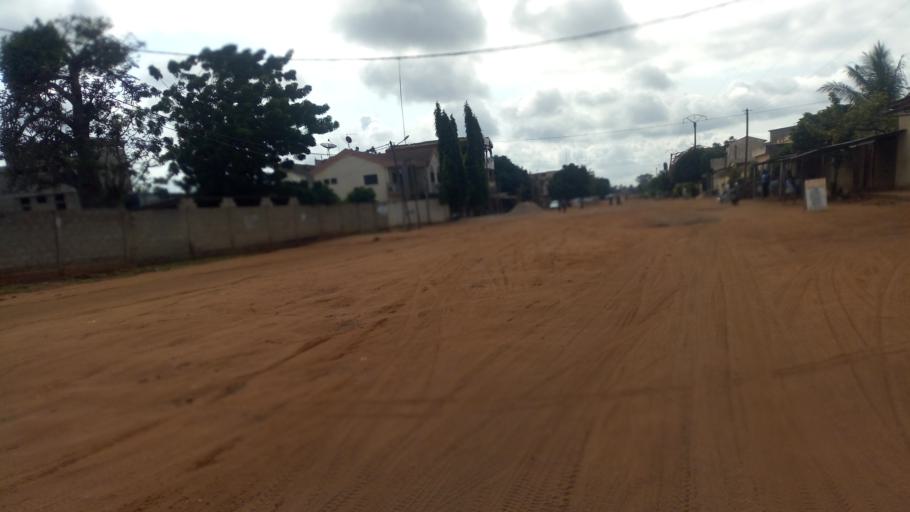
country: TG
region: Maritime
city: Lome
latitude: 6.2190
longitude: 1.1917
